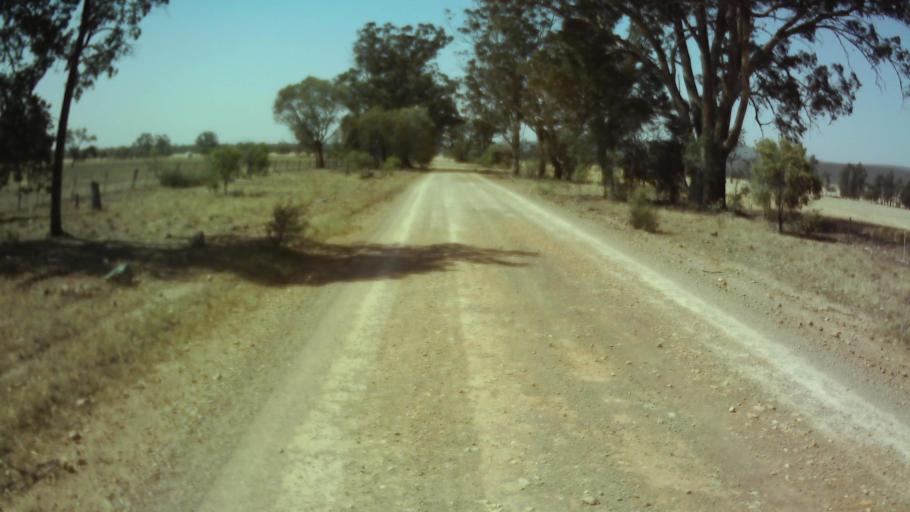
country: AU
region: New South Wales
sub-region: Weddin
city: Grenfell
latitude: -33.9901
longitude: 147.9266
